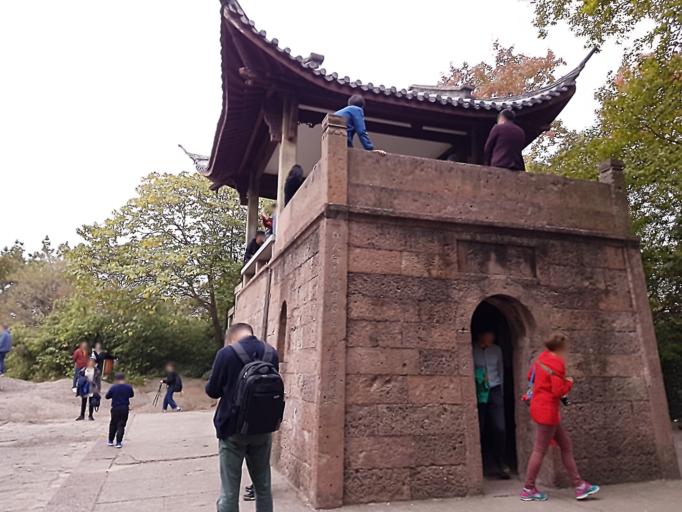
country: CN
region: Zhejiang Sheng
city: Gudang
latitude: 30.2615
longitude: 120.1371
